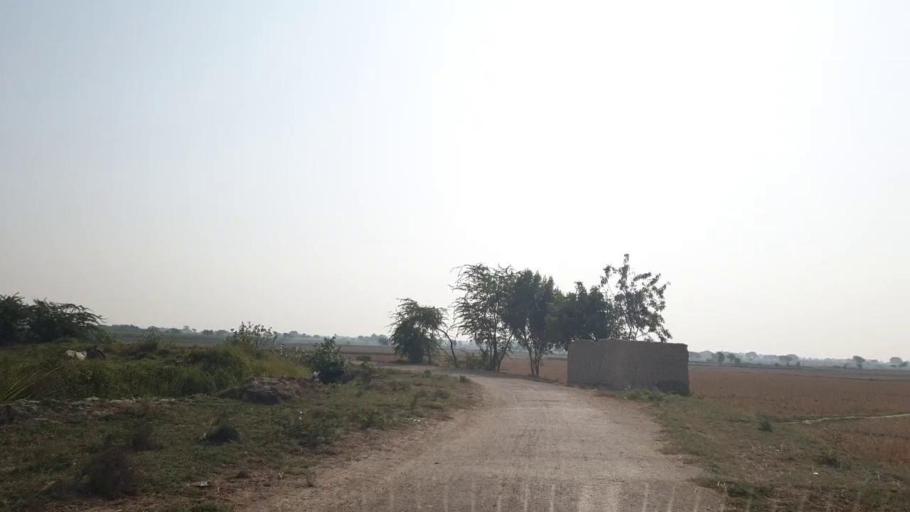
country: PK
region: Sindh
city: Matli
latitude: 25.0048
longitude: 68.6245
